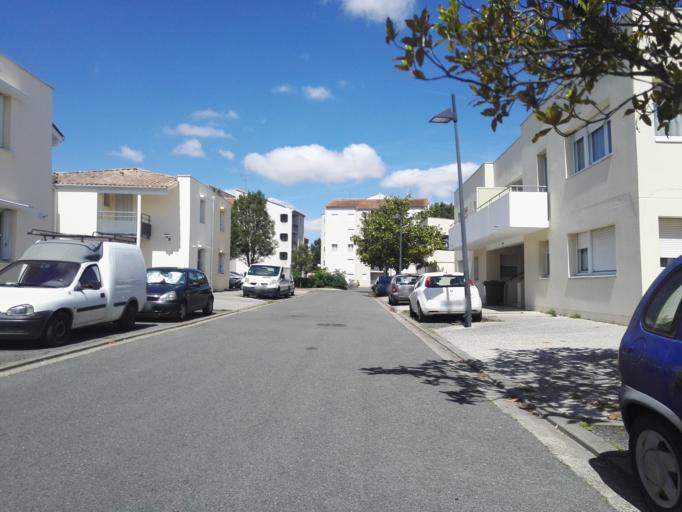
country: FR
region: Aquitaine
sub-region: Departement de la Gironde
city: Begles
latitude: 44.8007
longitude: -0.5393
